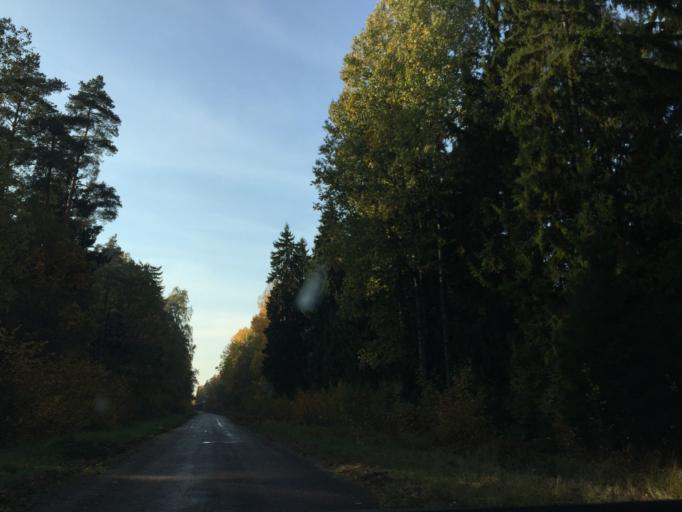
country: LV
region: Skrunda
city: Skrunda
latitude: 56.6790
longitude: 22.1509
